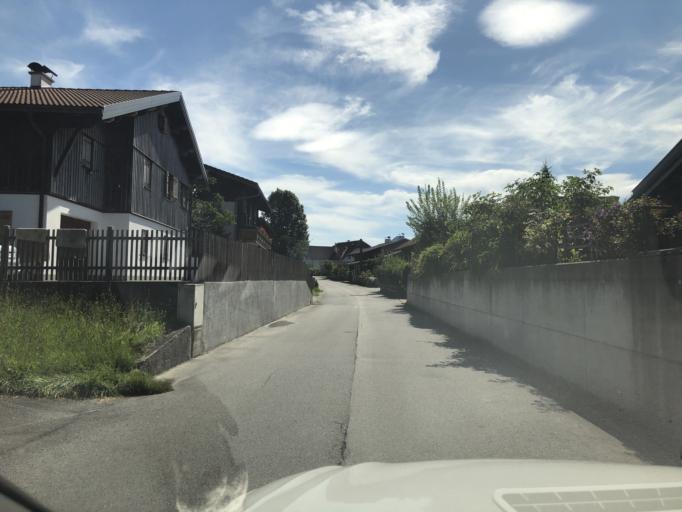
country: AT
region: Salzburg
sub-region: Politischer Bezirk Salzburg-Umgebung
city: Plainfeld
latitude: 47.8269
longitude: 13.1898
